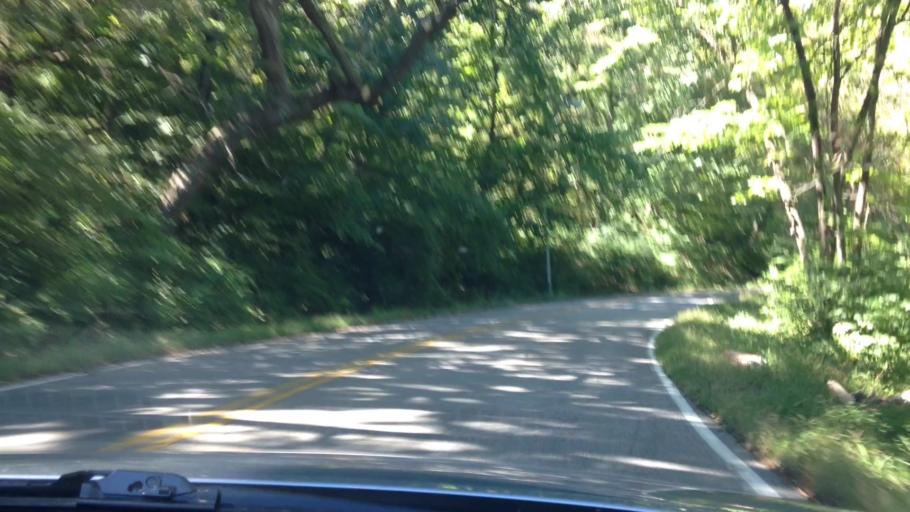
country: US
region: Missouri
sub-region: Jackson County
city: Raytown
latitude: 39.0030
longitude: -94.5133
